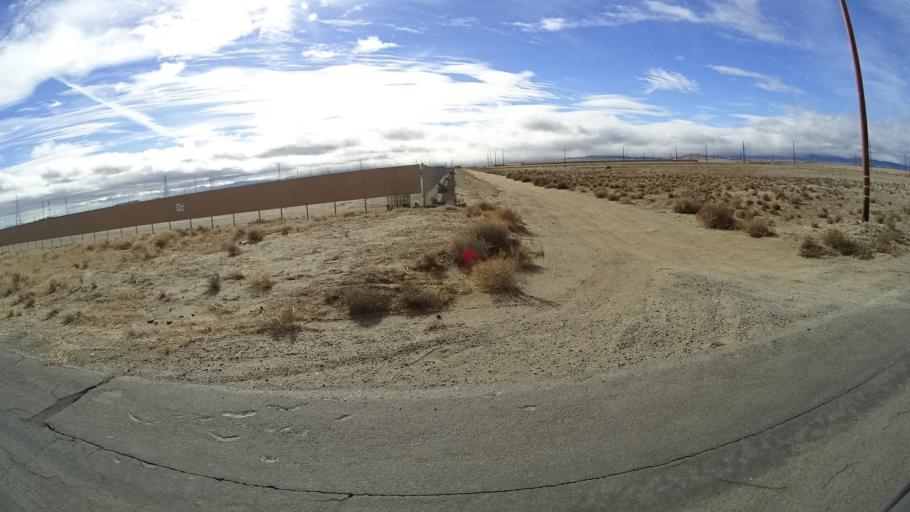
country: US
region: California
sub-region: Kern County
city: Rosamond
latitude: 34.8341
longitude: -118.3437
